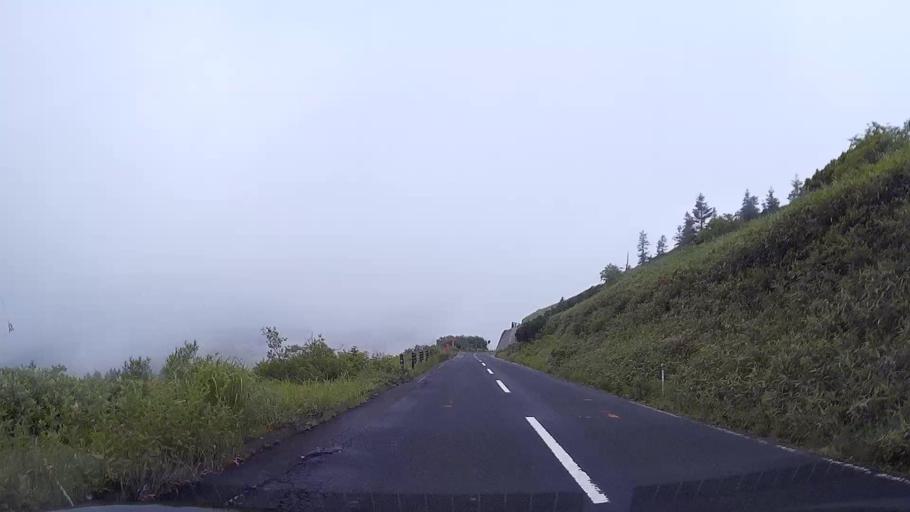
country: JP
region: Nagano
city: Nakano
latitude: 36.6567
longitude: 138.5298
